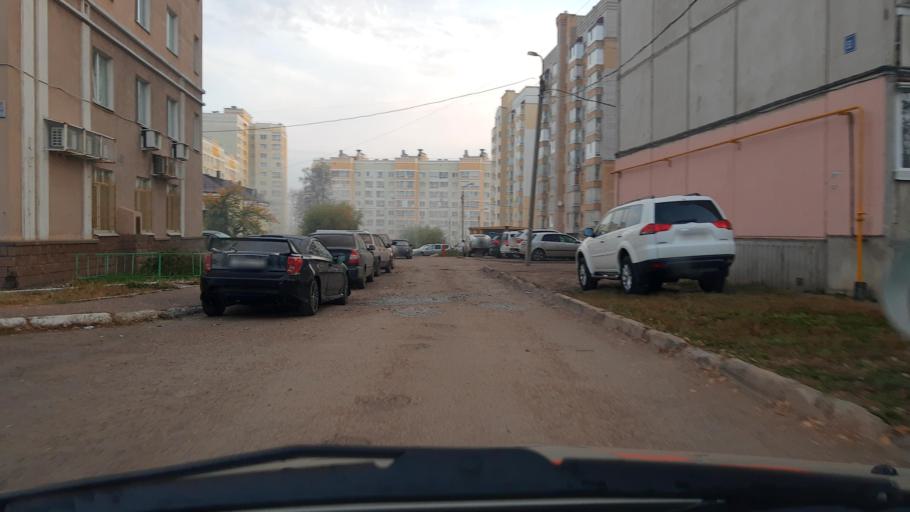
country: RU
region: Bashkortostan
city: Ufa
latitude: 54.8230
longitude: 56.0772
